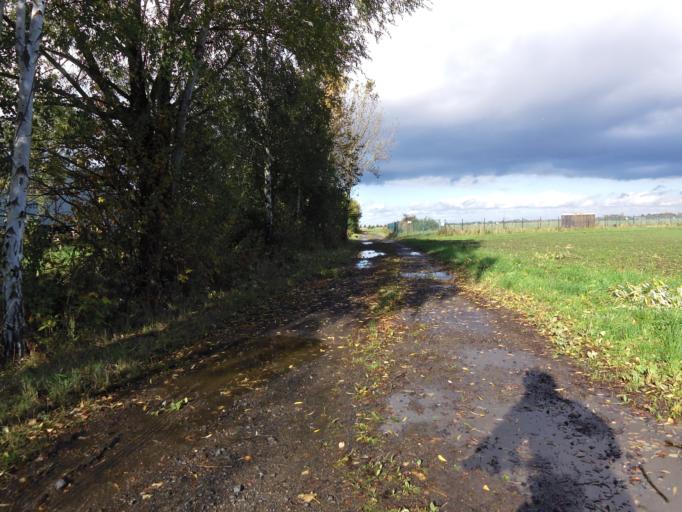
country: DE
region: Saxony
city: Borsdorf
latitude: 51.3204
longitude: 12.4950
